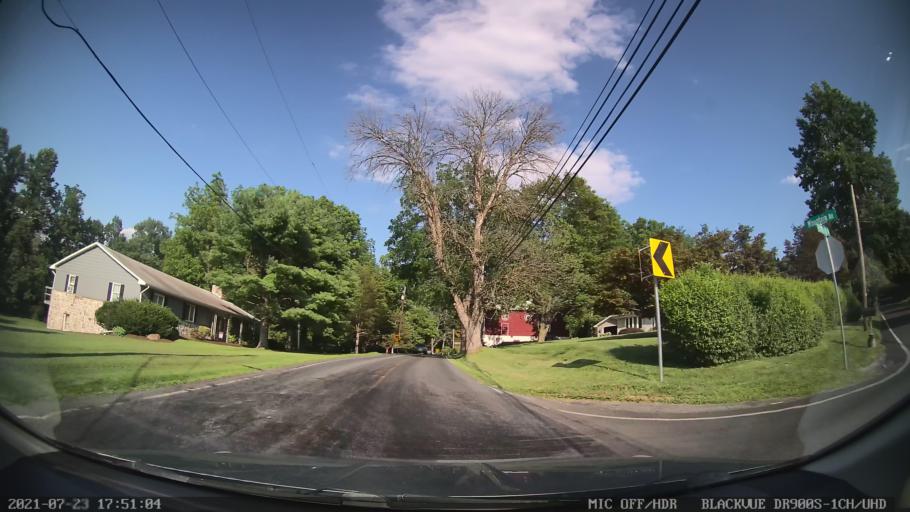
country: US
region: Pennsylvania
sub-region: Lehigh County
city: Alburtis
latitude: 40.4946
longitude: -75.5896
